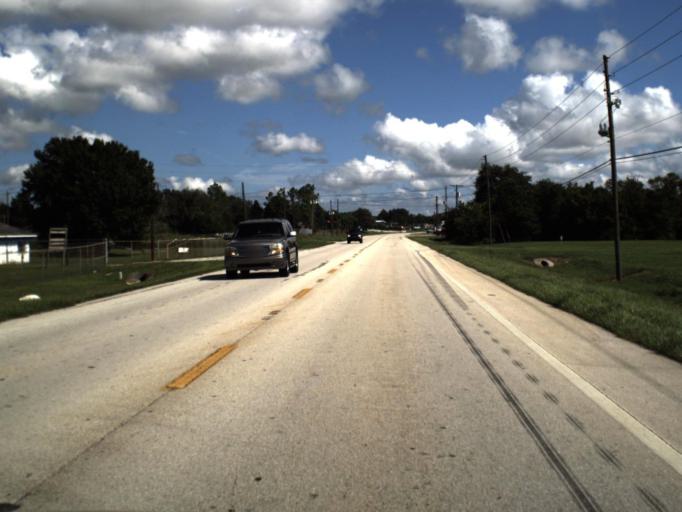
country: US
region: Florida
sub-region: Polk County
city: Davenport
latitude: 28.1437
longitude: -81.6118
